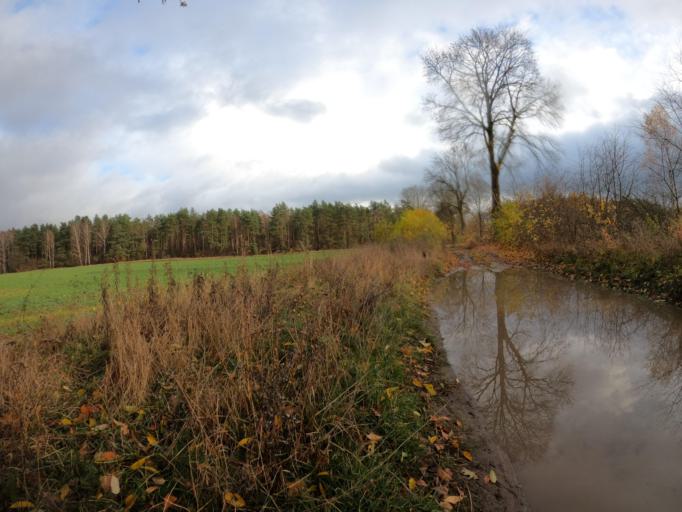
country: PL
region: West Pomeranian Voivodeship
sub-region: Powiat walecki
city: Tuczno
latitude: 53.2349
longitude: 16.2510
